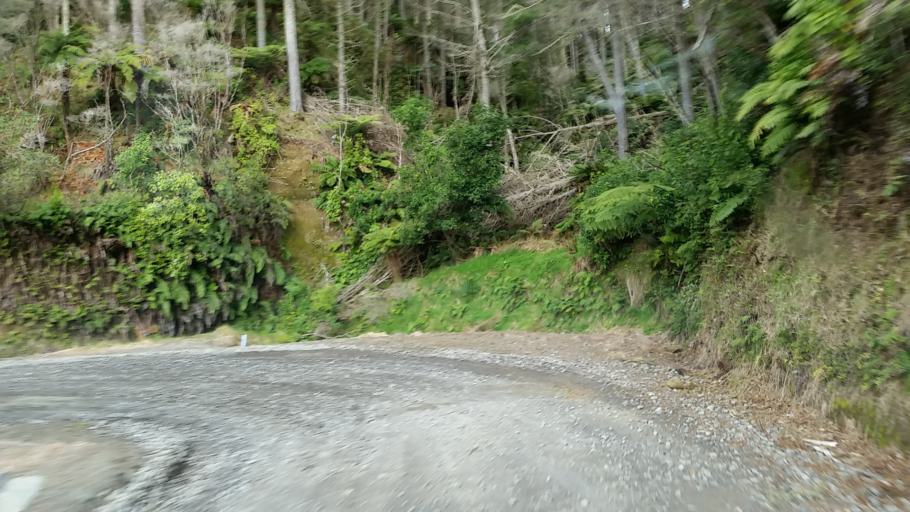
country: NZ
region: Taranaki
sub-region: New Plymouth District
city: Waitara
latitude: -39.1587
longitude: 174.5562
